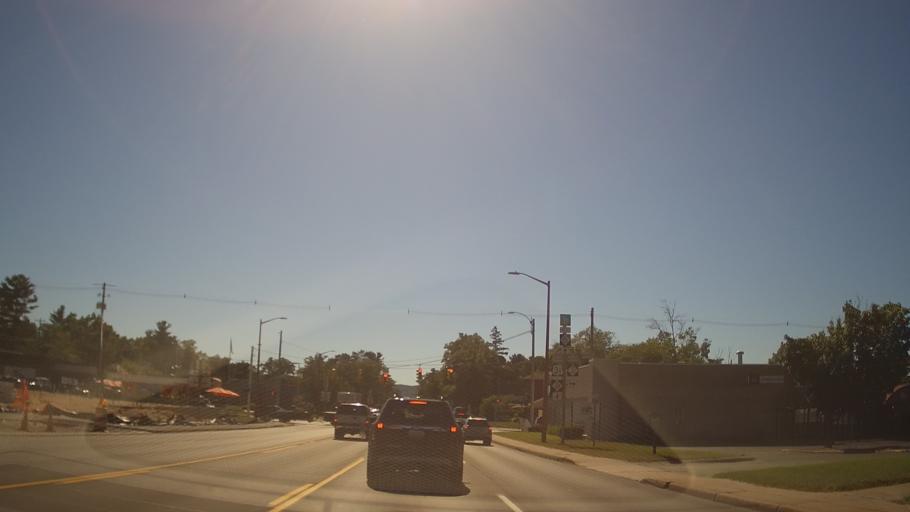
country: US
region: Michigan
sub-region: Grand Traverse County
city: Traverse City
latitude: 44.7642
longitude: -85.5941
